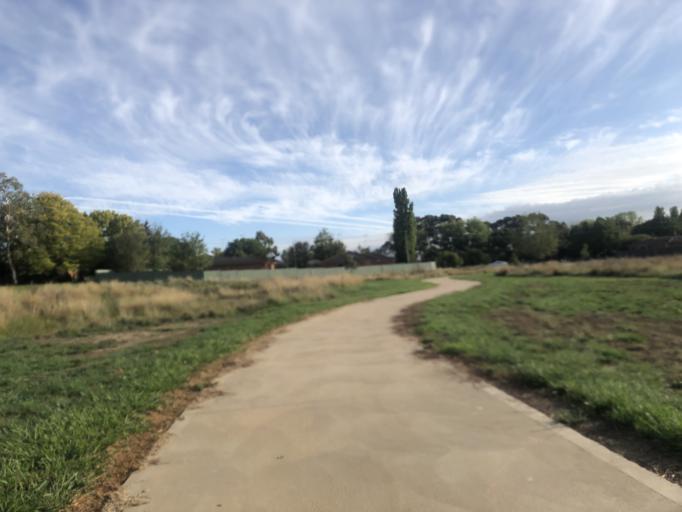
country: AU
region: New South Wales
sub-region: Orange Municipality
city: Orange
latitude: -33.2948
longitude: 149.0925
